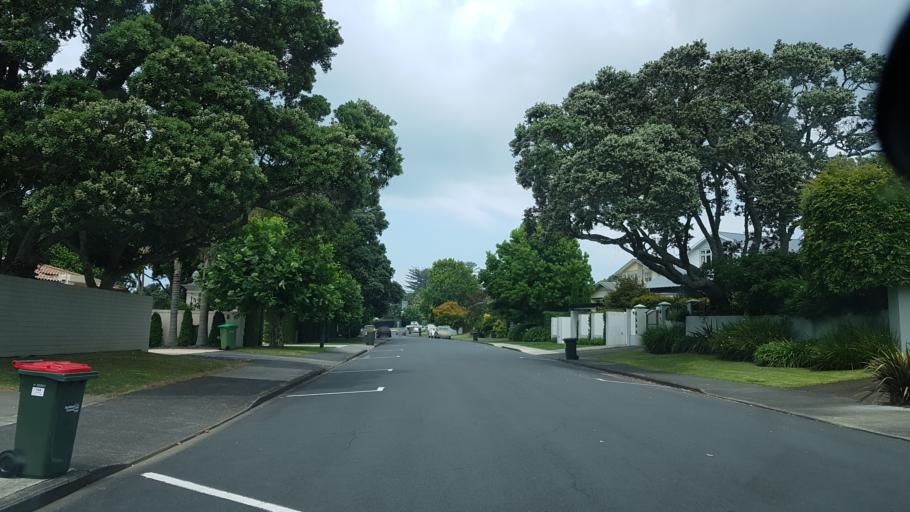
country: NZ
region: Auckland
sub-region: Auckland
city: North Shore
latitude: -36.7965
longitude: 174.7837
